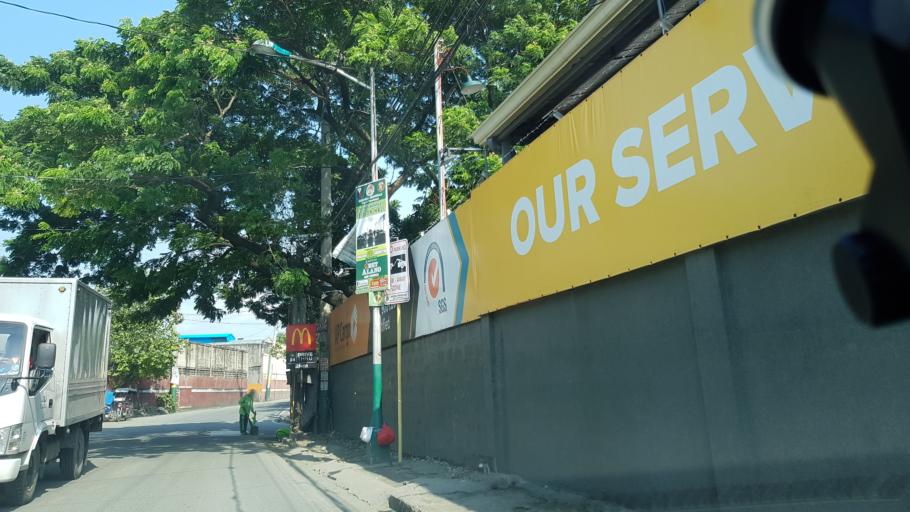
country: PH
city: Sambayanihan People's Village
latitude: 14.4997
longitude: 121.0101
